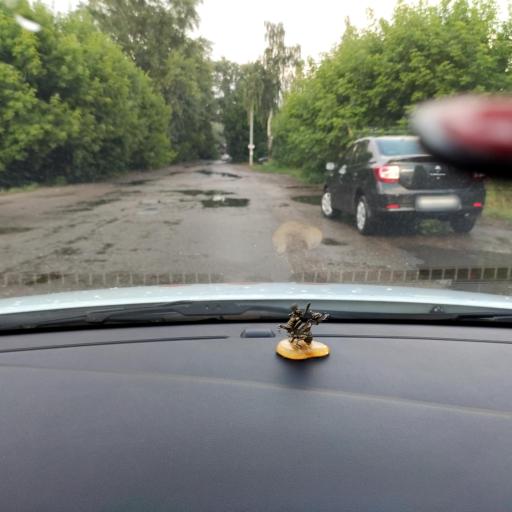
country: RU
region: Tatarstan
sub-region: Zelenodol'skiy Rayon
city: Zelenodolsk
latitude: 55.8412
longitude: 48.5619
